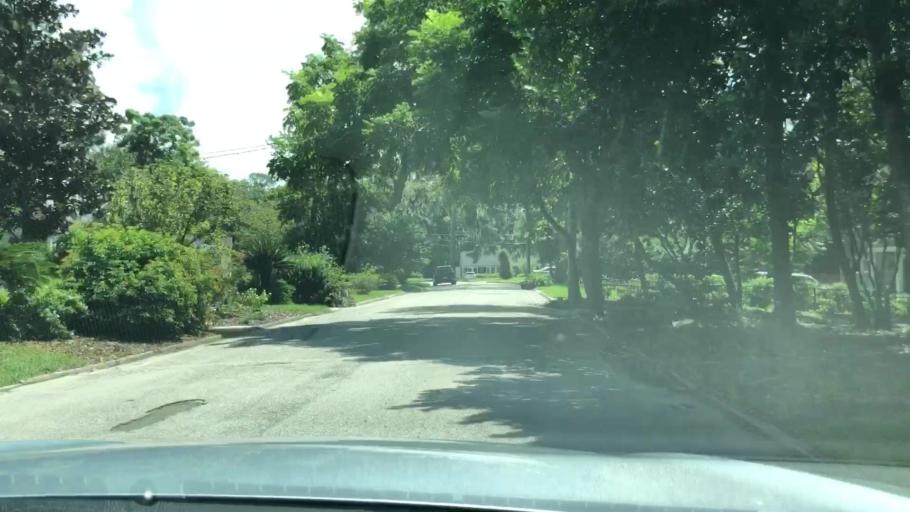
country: US
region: Florida
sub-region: Duval County
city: Jacksonville
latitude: 30.2836
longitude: -81.6533
